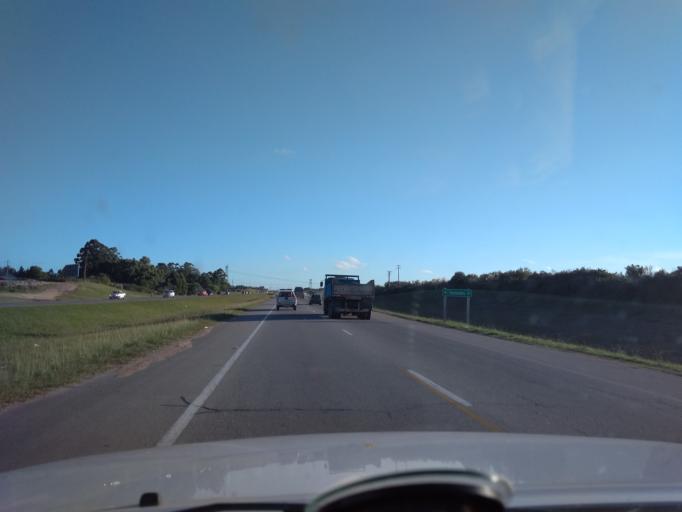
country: UY
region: Canelones
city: La Paz
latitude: -34.7552
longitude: -56.2586
